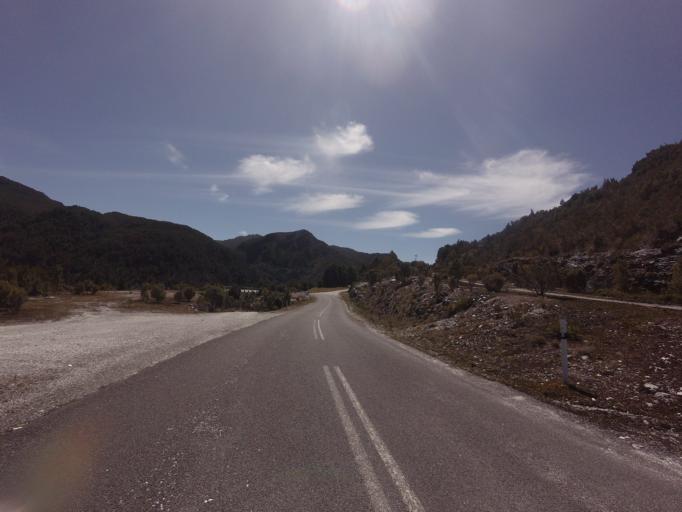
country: AU
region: Tasmania
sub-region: West Coast
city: Queenstown
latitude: -42.7343
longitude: 145.9757
